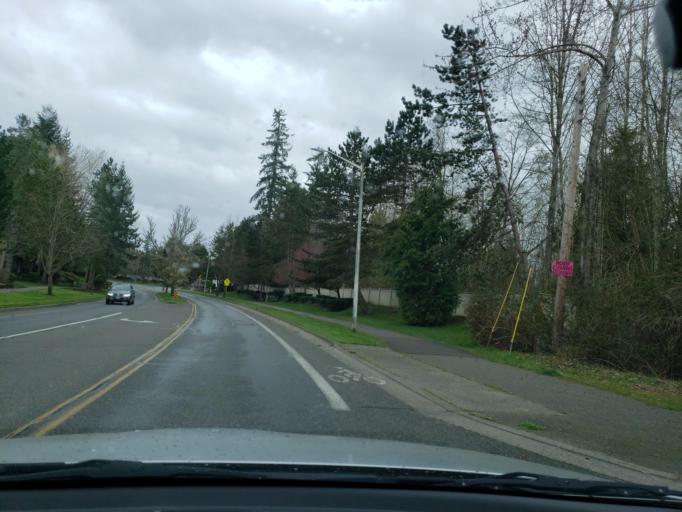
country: US
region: Washington
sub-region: Snohomish County
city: Meadowdale
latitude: 47.8871
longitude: -122.3098
